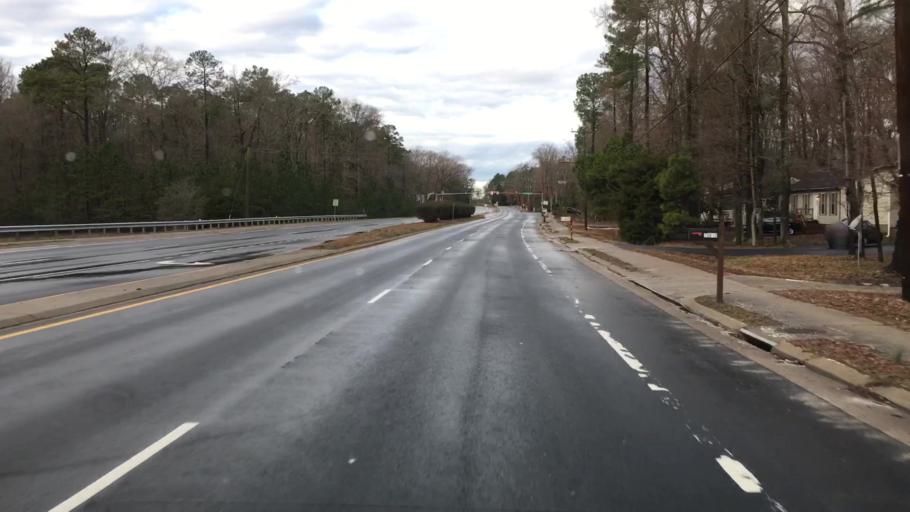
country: US
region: Virginia
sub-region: Chesterfield County
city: Bon Air
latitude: 37.5165
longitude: -77.5954
